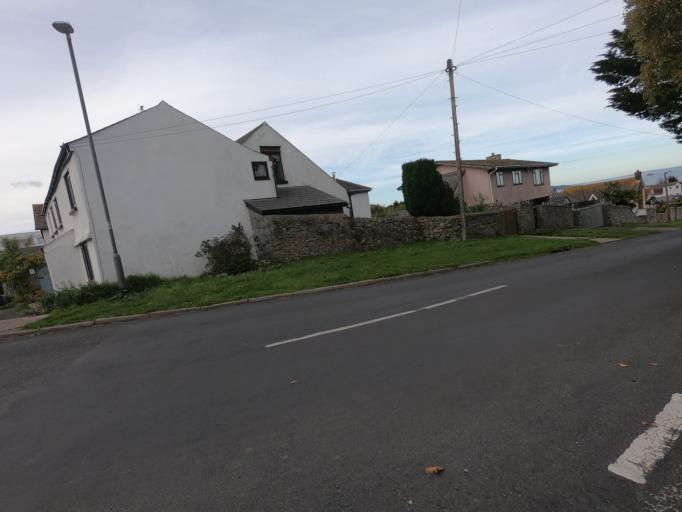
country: GB
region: England
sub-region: Borough of Torbay
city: Brixham
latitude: 50.3984
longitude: -3.4981
